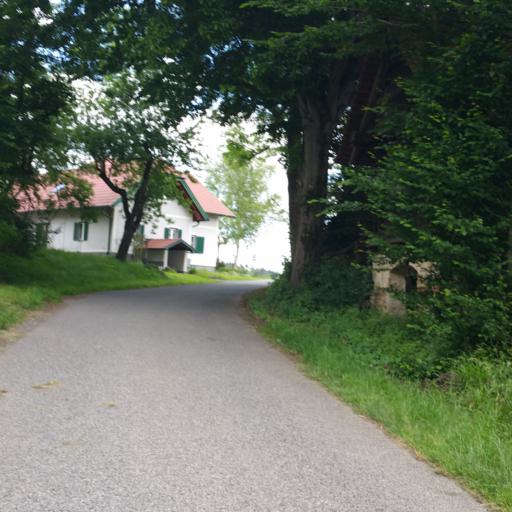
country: AT
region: Styria
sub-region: Politischer Bezirk Leibnitz
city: Gleinstatten
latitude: 46.7442
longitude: 15.3382
